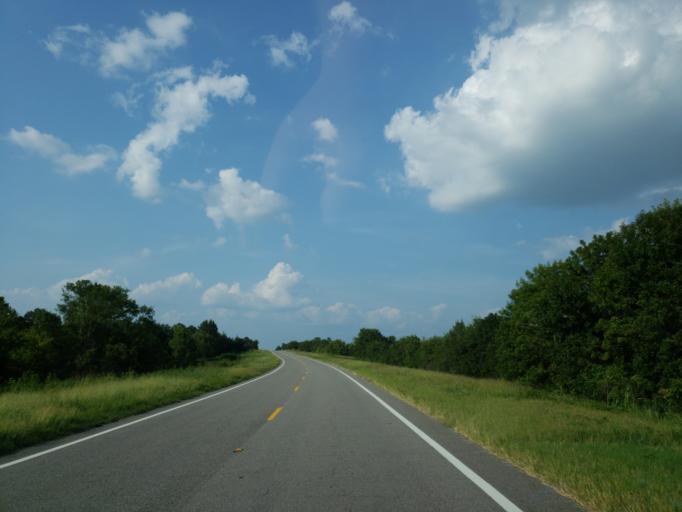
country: US
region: Alabama
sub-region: Greene County
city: Eutaw
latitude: 32.7832
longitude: -87.9777
